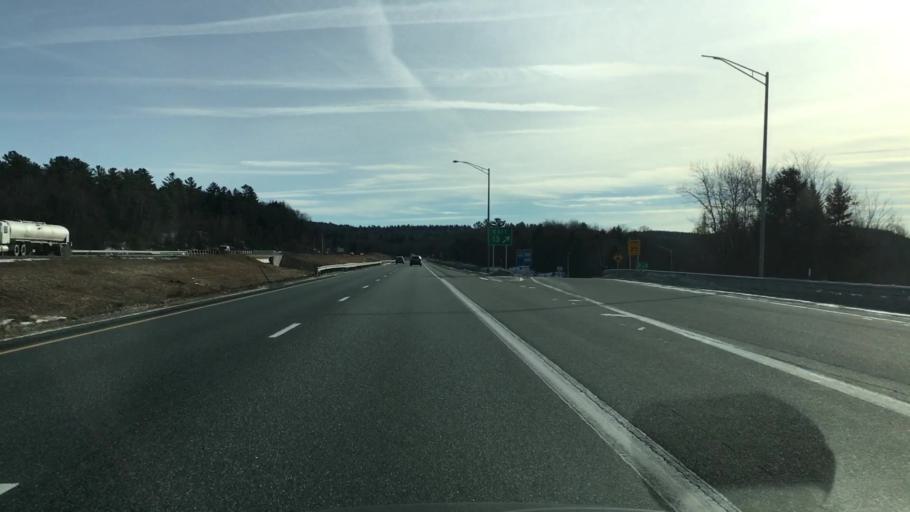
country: US
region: New Hampshire
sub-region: Sullivan County
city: Grantham
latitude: 43.5004
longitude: -72.1337
